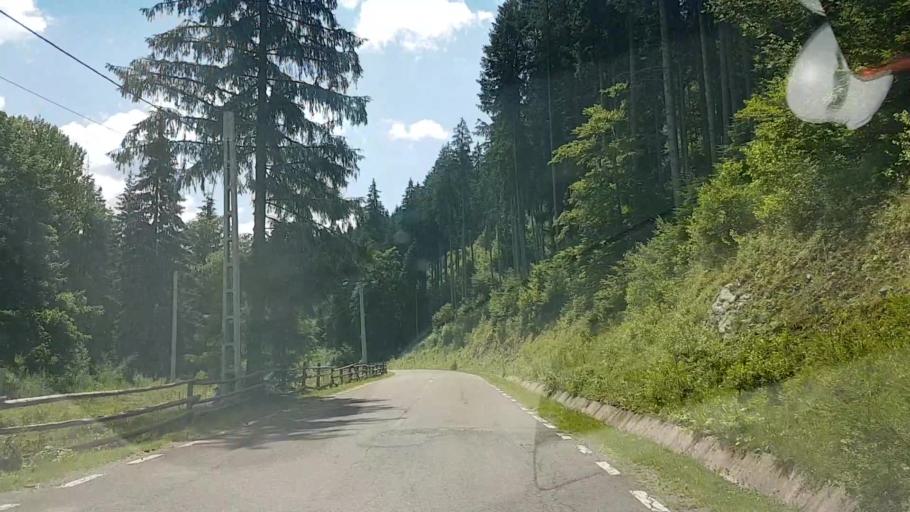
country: RO
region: Suceava
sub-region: Comuna Sadova
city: Sadova
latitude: 47.4804
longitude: 25.4931
